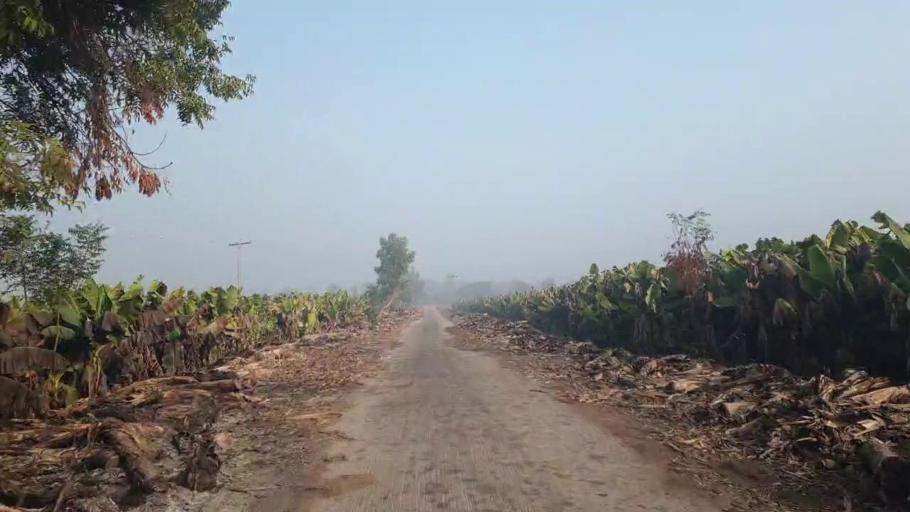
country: PK
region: Sindh
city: Tando Adam
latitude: 25.8064
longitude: 68.6333
